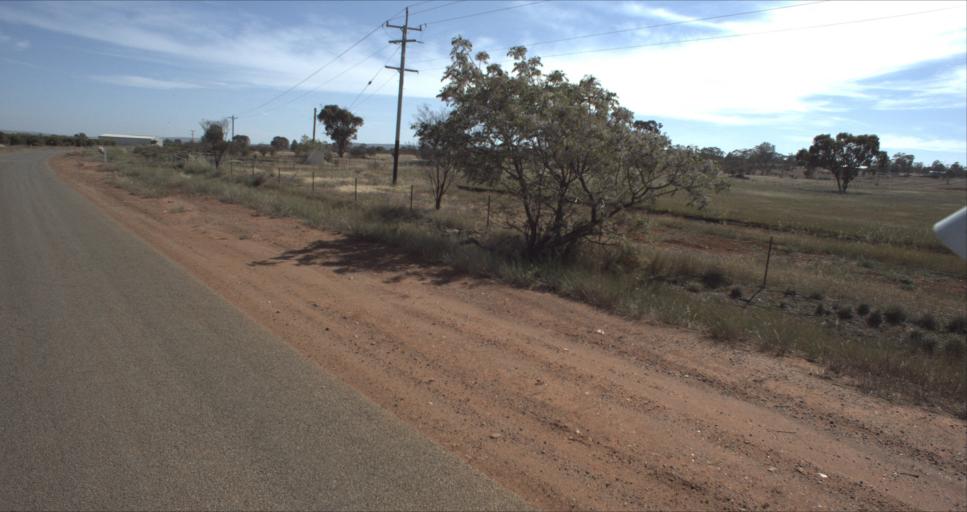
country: AU
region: New South Wales
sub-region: Leeton
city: Leeton
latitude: -34.5860
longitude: 146.4769
